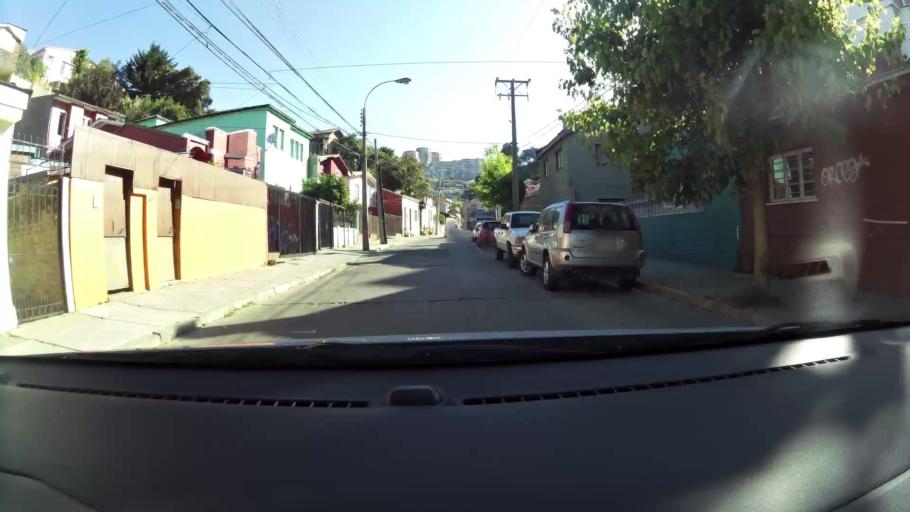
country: CL
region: Valparaiso
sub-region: Provincia de Valparaiso
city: Vina del Mar
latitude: -33.0306
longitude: -71.5623
